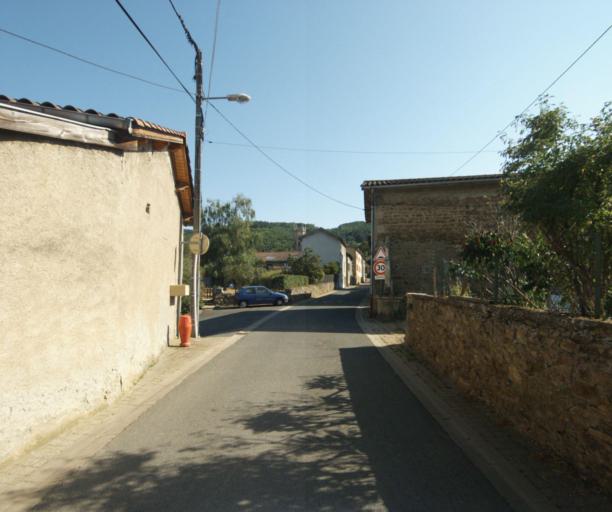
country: FR
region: Rhone-Alpes
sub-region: Departement du Rhone
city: Saint-Pierre-la-Palud
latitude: 45.7717
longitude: 4.6079
